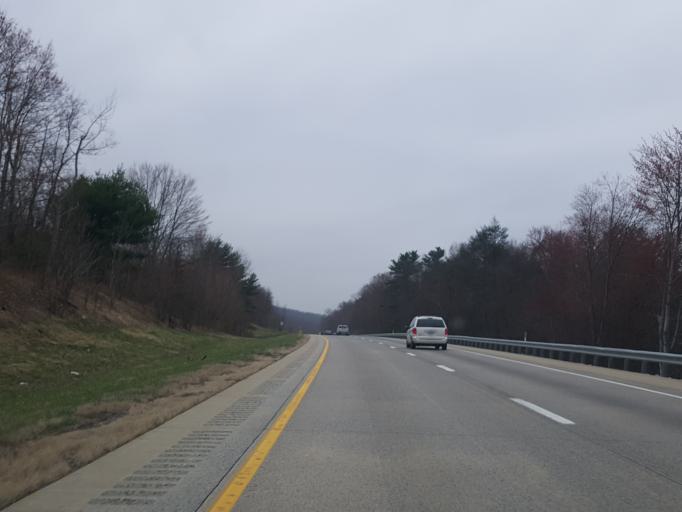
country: US
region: Pennsylvania
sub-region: Lebanon County
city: Jonestown
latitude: 40.5048
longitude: -76.4995
